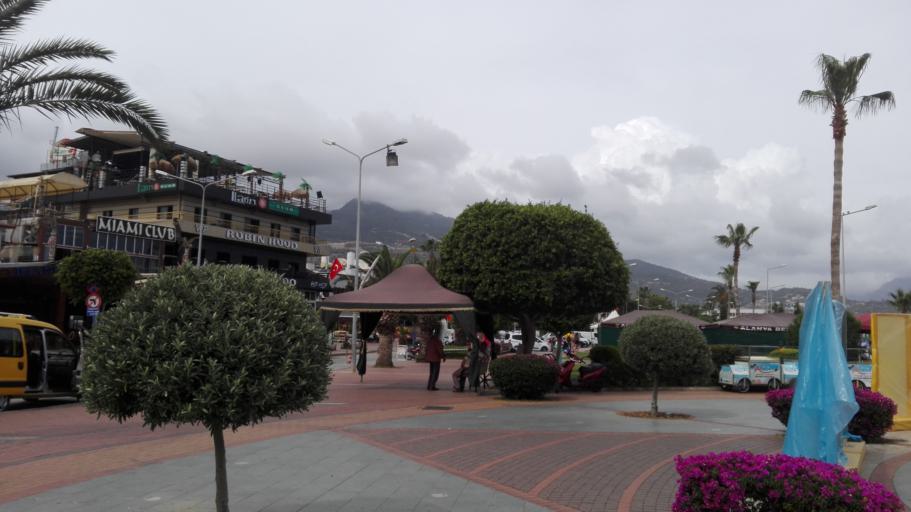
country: TR
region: Antalya
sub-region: Alanya
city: Alanya
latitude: 36.5403
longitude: 31.9990
